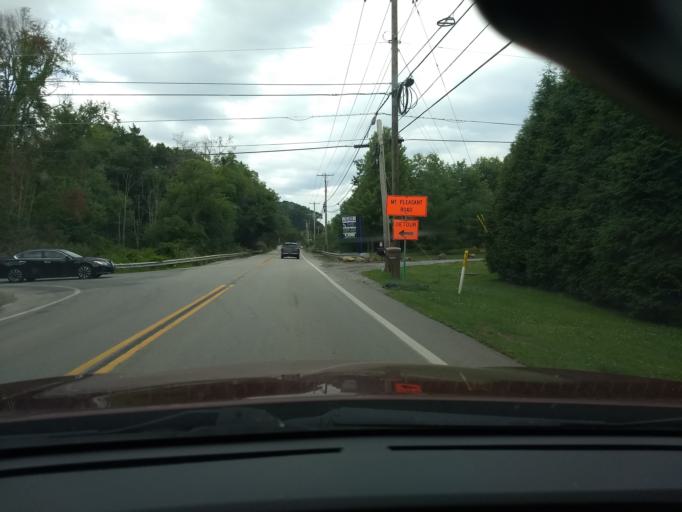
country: US
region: Pennsylvania
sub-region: Allegheny County
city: Bradford Woods
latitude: 40.6534
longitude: -80.0682
